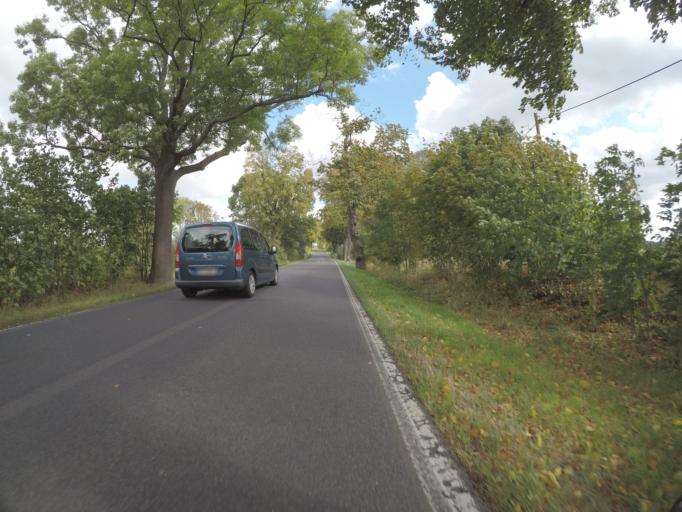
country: DE
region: Brandenburg
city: Altlandsberg
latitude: 52.5778
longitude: 13.7540
